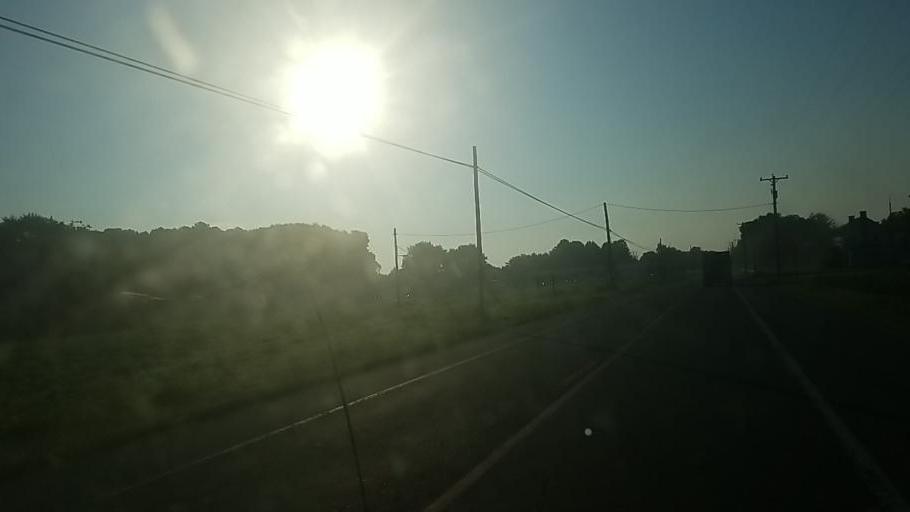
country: US
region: Maryland
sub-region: Worcester County
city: Ocean Pines
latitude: 38.4620
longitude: -75.1407
